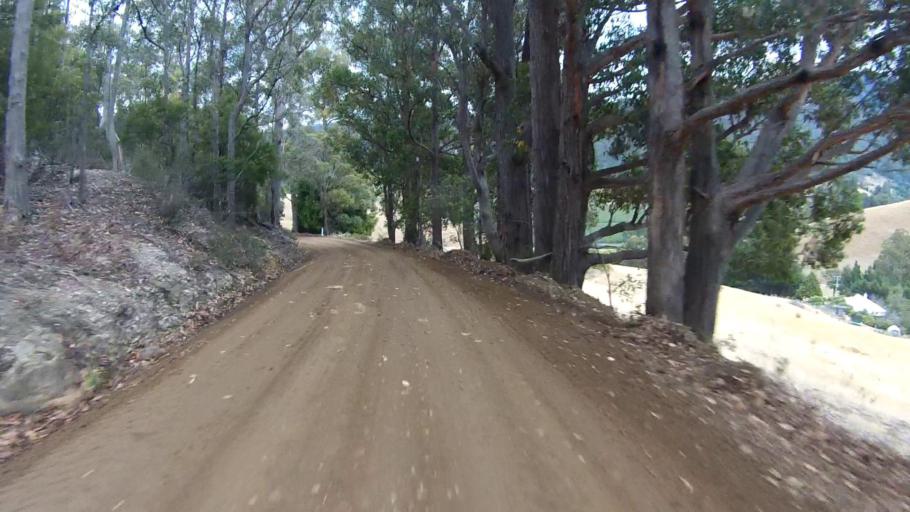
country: AU
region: Tasmania
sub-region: Huon Valley
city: Huonville
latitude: -42.9673
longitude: 147.0460
